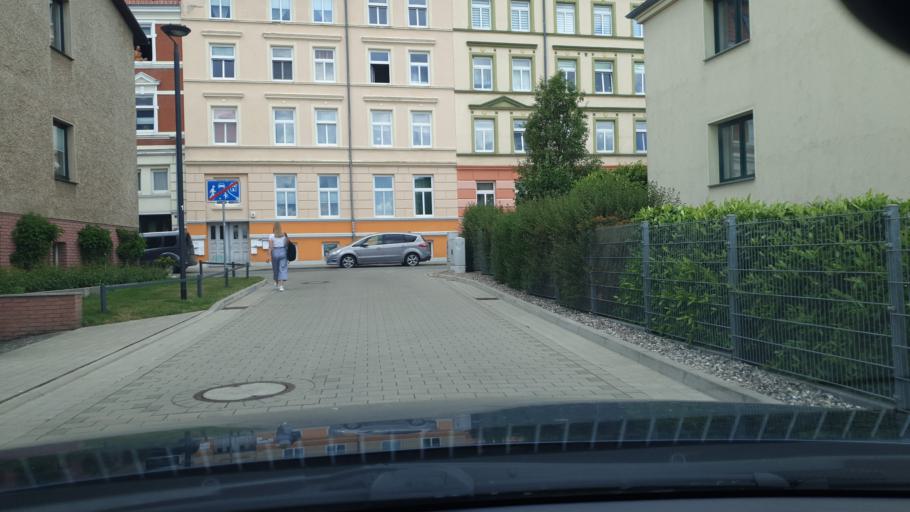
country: DE
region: Mecklenburg-Vorpommern
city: Werdervorstadt
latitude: 53.6346
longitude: 11.4291
